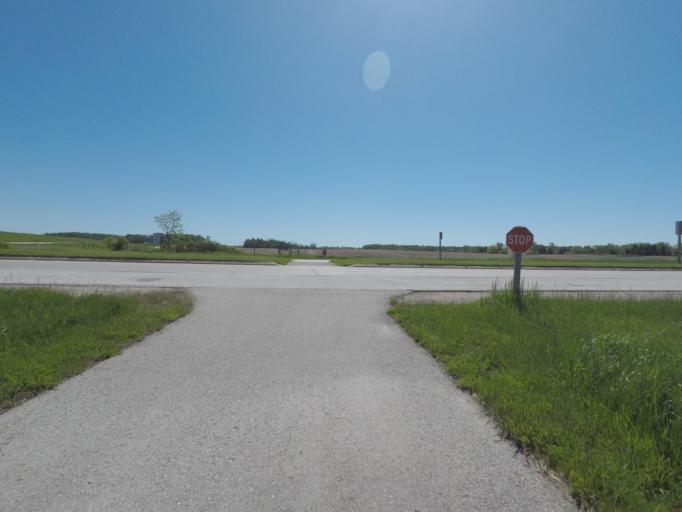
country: US
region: Wisconsin
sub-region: Sheboygan County
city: Sheboygan Falls
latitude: 43.7492
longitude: -87.8201
